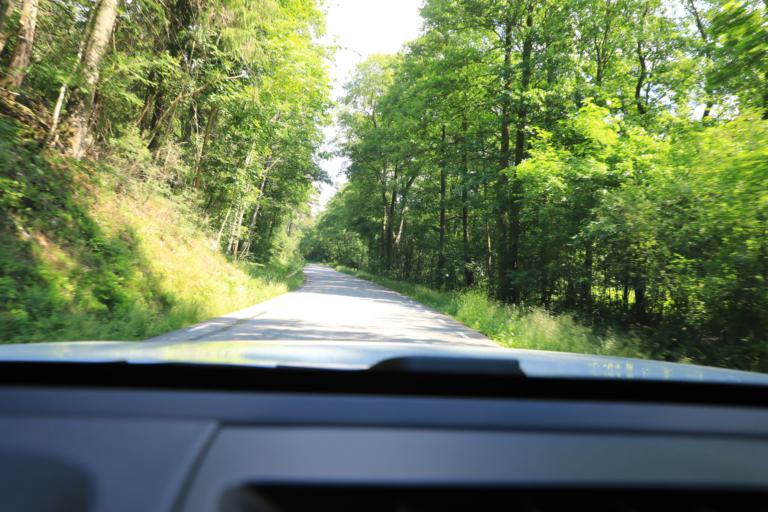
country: SE
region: Halland
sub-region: Varbergs Kommun
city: Veddige
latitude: 57.2049
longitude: 12.3388
